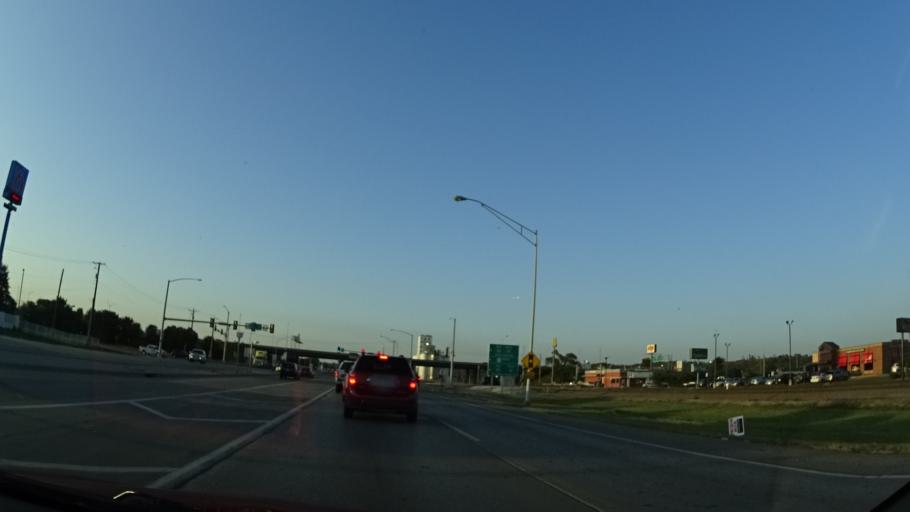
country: US
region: Iowa
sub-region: Pottawattamie County
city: Council Bluffs
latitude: 41.2297
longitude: -95.8513
